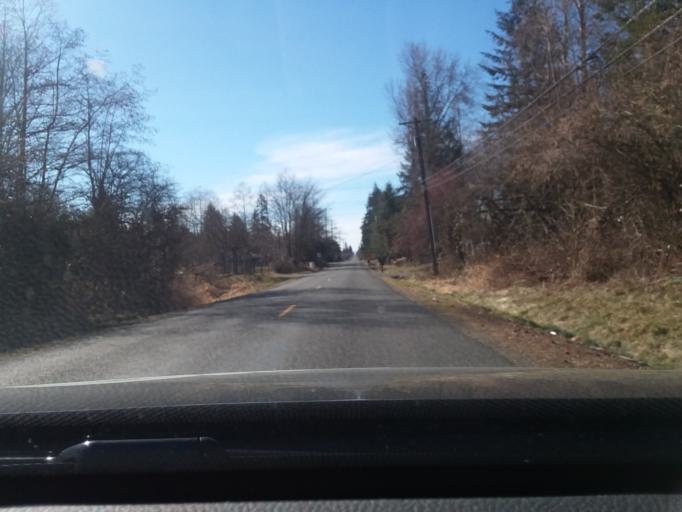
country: US
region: Washington
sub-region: Pierce County
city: Waller
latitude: 47.1827
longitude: -122.3786
